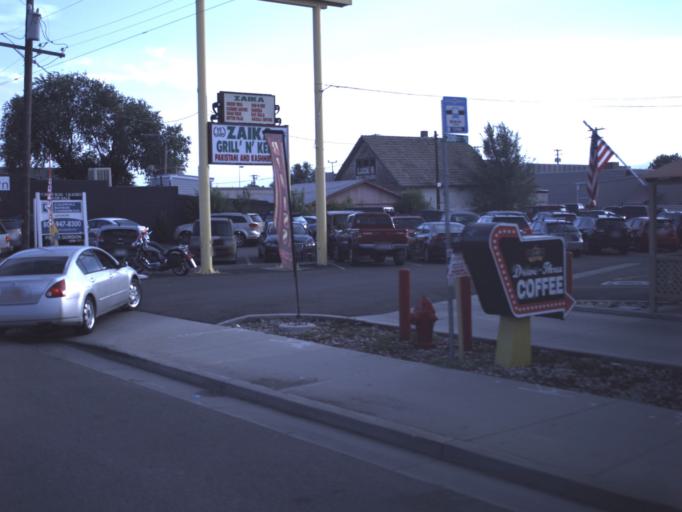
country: US
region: Utah
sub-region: Salt Lake County
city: Centerfield
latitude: 40.6945
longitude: -111.8884
